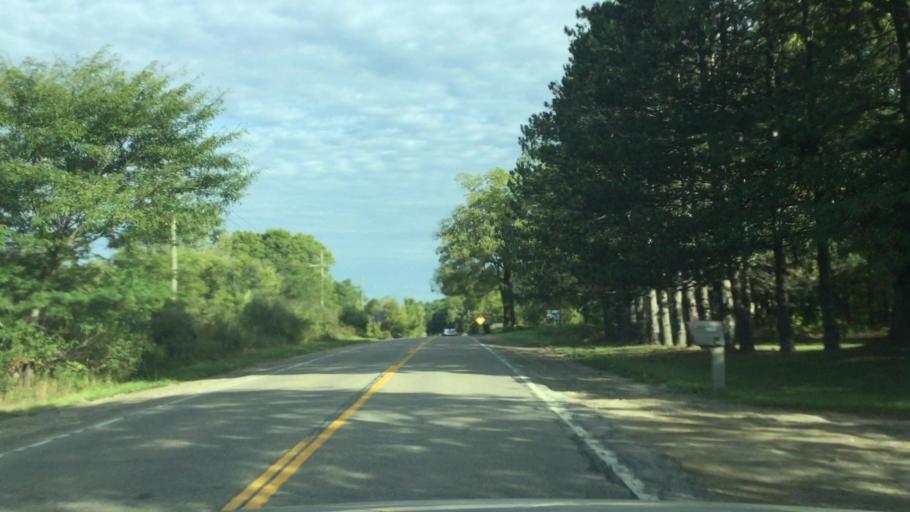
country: US
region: Michigan
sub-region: Livingston County
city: Howell
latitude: 42.5885
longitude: -83.9000
